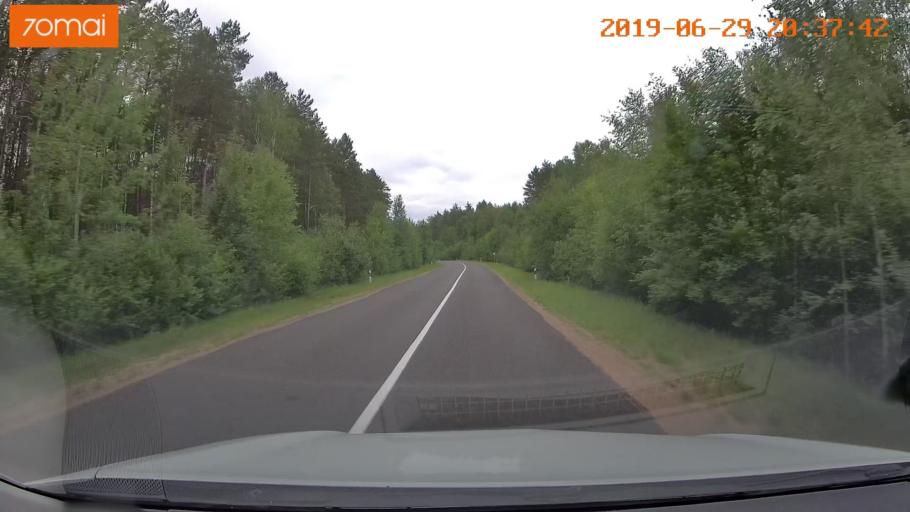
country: BY
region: Brest
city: Hantsavichy
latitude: 52.5414
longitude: 26.3655
